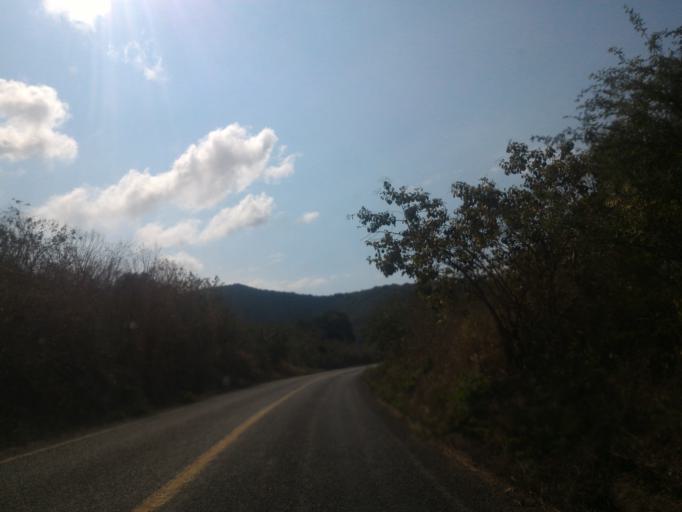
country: MX
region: Michoacan
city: Coahuayana Viejo
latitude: 18.5000
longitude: -103.5713
